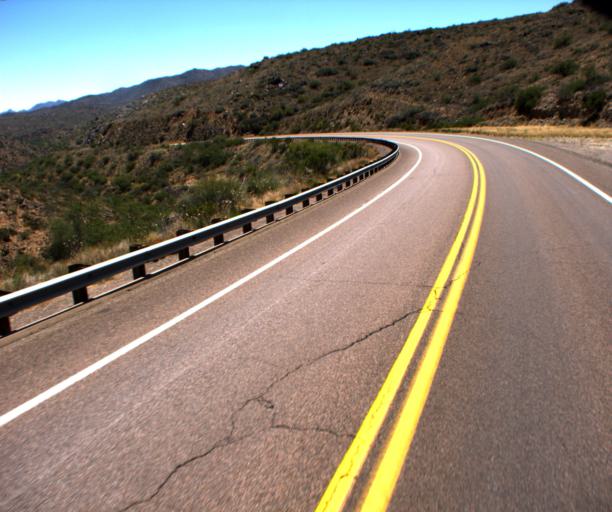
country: US
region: Arizona
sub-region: Yavapai County
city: Bagdad
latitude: 34.5410
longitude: -113.1471
